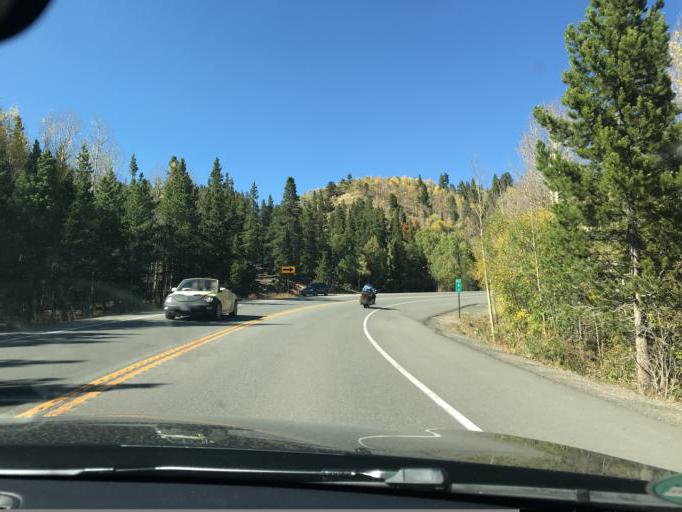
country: US
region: Colorado
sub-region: Boulder County
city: Nederland
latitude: 40.0681
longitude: -105.5165
